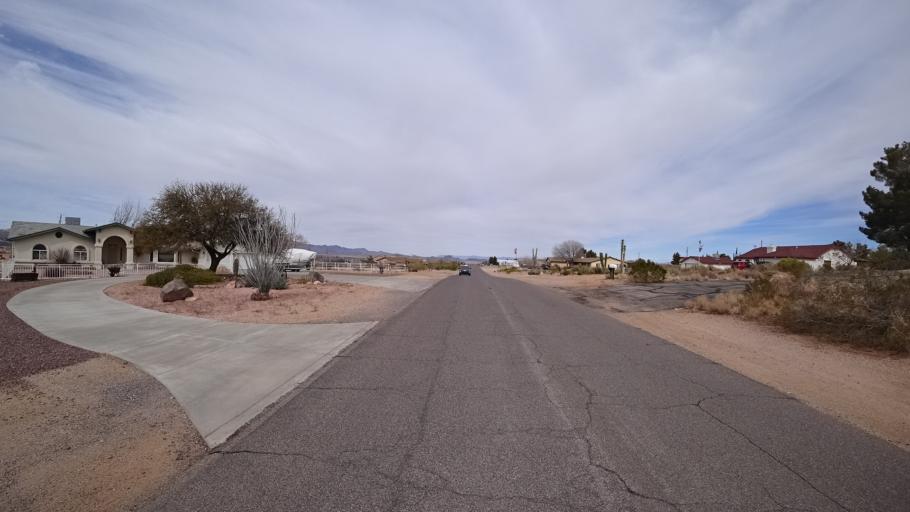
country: US
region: Arizona
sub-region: Mohave County
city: Kingman
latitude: 35.1831
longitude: -113.9928
